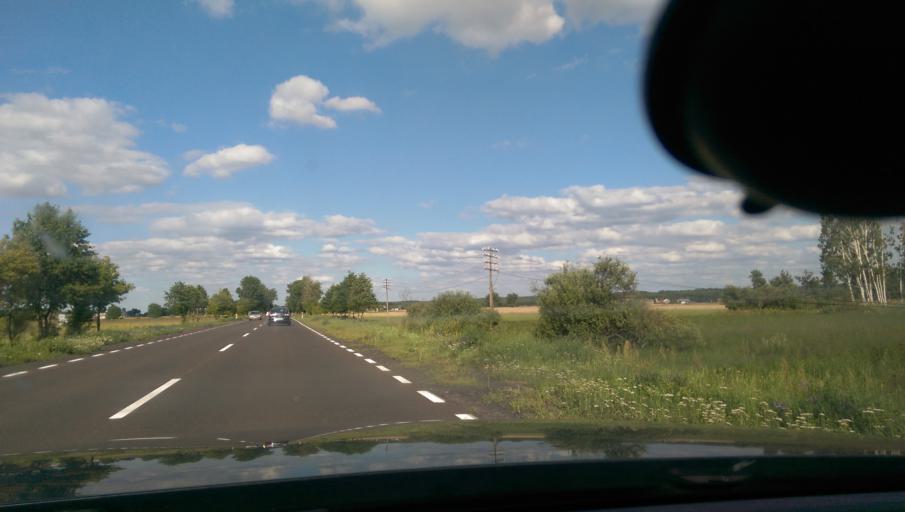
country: PL
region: Lubusz
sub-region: Powiat sulecinski
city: Krzeszyce
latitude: 52.5670
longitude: 14.9700
